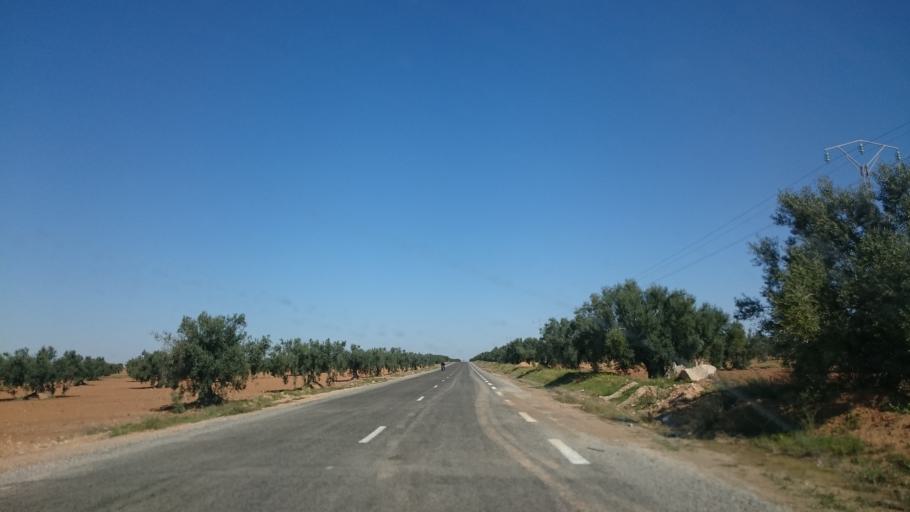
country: TN
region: Safaqis
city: Sfax
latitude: 34.8403
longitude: 10.4572
